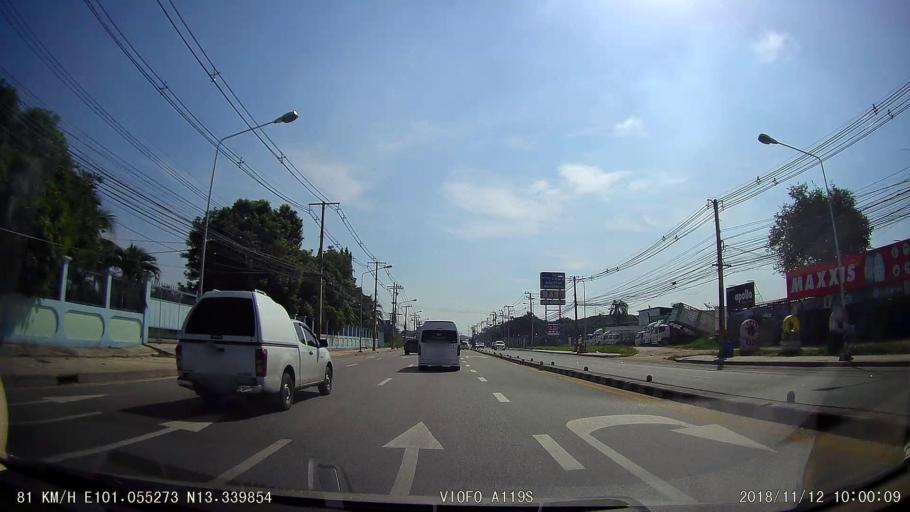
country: TH
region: Chon Buri
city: Ban Bueng
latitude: 13.3398
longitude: 101.0554
